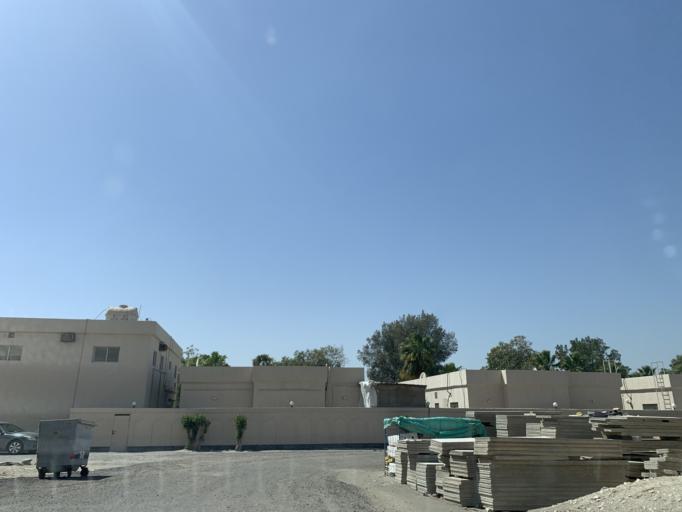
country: BH
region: Manama
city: Manama
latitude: 26.1980
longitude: 50.5641
